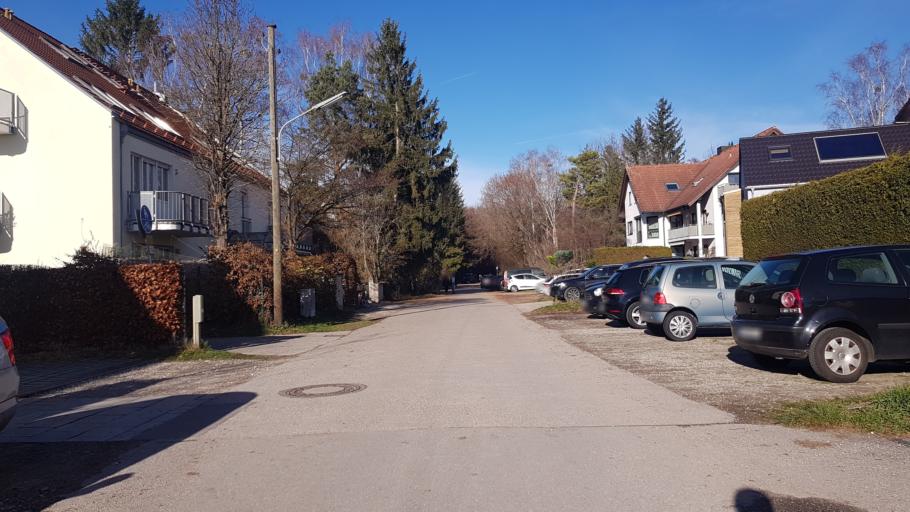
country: DE
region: Bavaria
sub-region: Upper Bavaria
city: Karlsfeld
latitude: 48.1896
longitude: 11.5124
